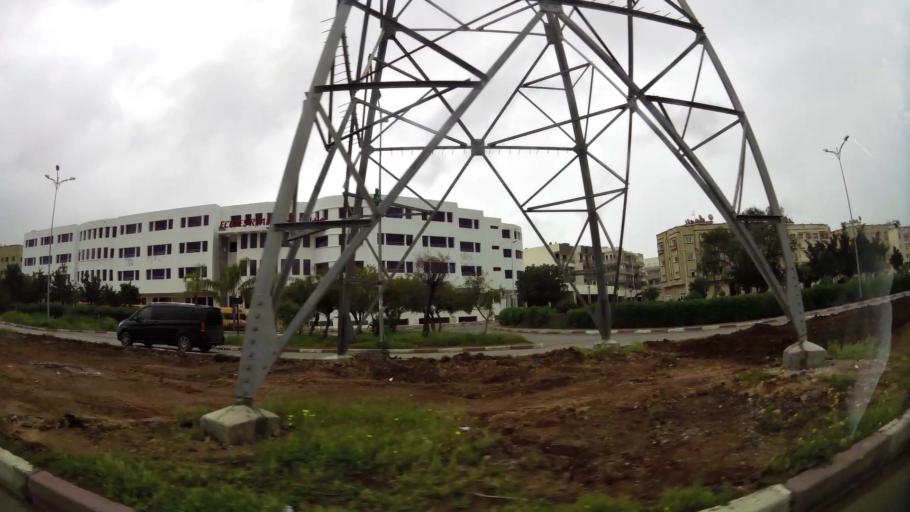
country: MA
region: Grand Casablanca
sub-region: Casablanca
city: Casablanca
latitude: 33.5287
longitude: -7.6166
